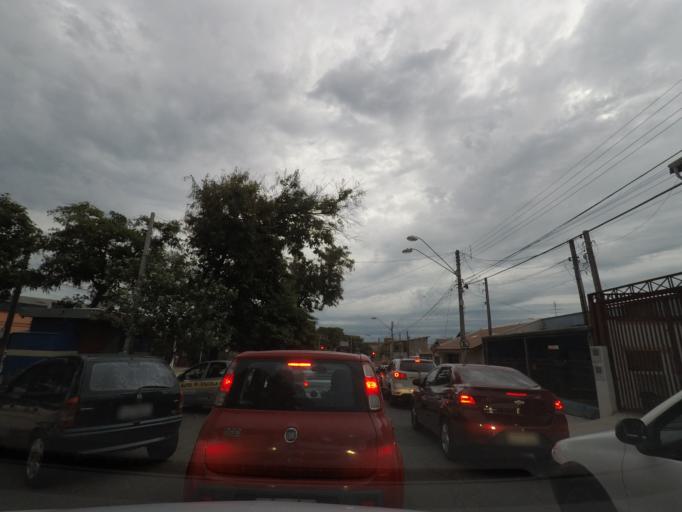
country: BR
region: Sao Paulo
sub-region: Campinas
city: Campinas
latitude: -22.9334
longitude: -47.0921
